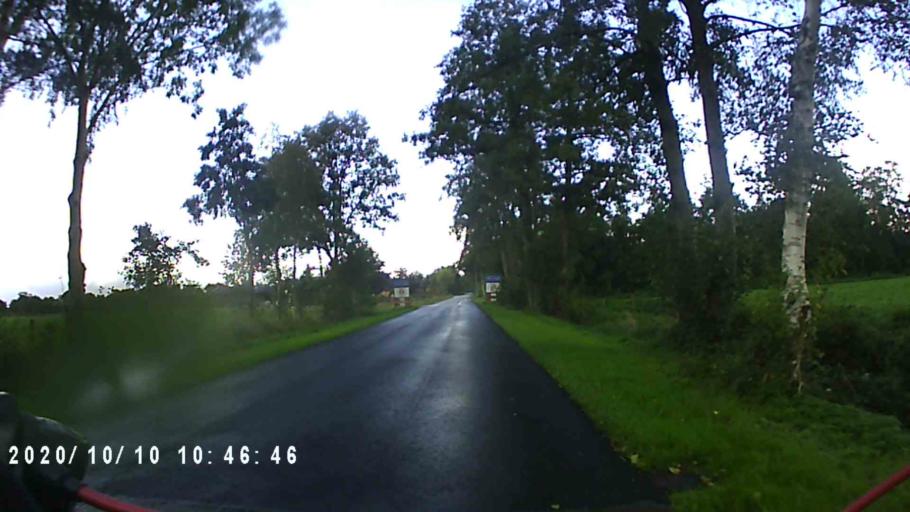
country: NL
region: Groningen
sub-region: Gemeente Grootegast
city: Grootegast
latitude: 53.1677
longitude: 6.2507
